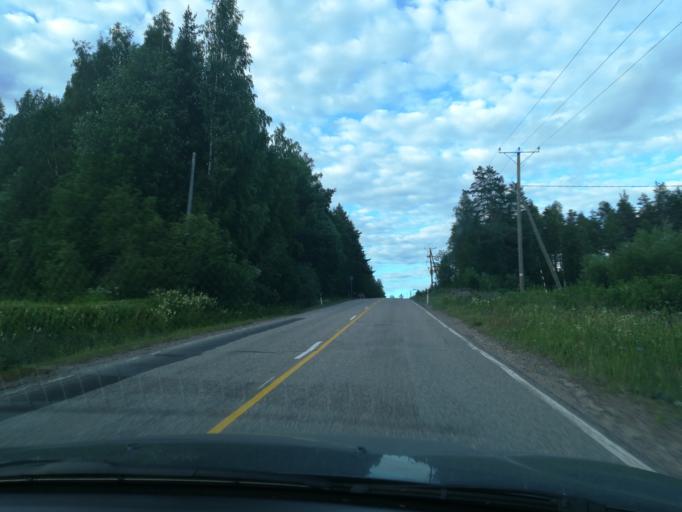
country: FI
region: Southern Savonia
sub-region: Mikkeli
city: Puumala
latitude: 61.5674
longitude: 28.1233
